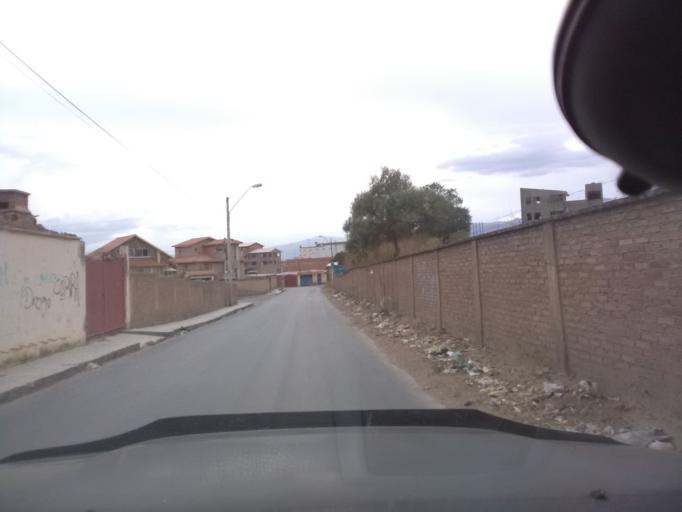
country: BO
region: Cochabamba
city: Cochabamba
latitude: -17.3510
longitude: -66.1880
